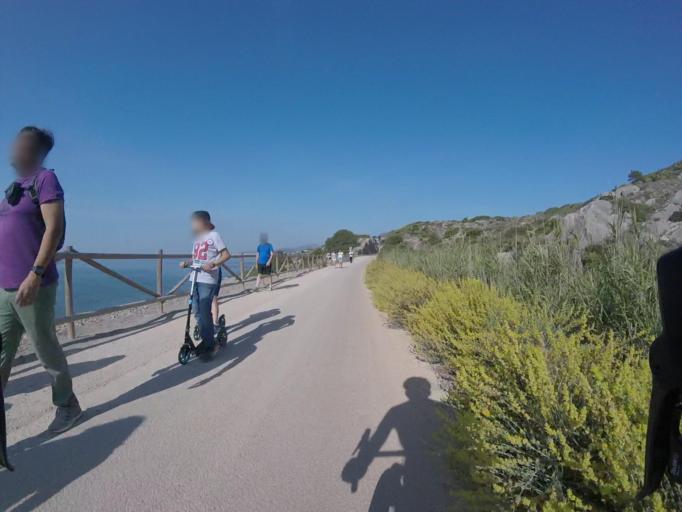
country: ES
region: Valencia
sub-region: Provincia de Castello
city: Benicassim
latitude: 40.0573
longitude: 0.1049
